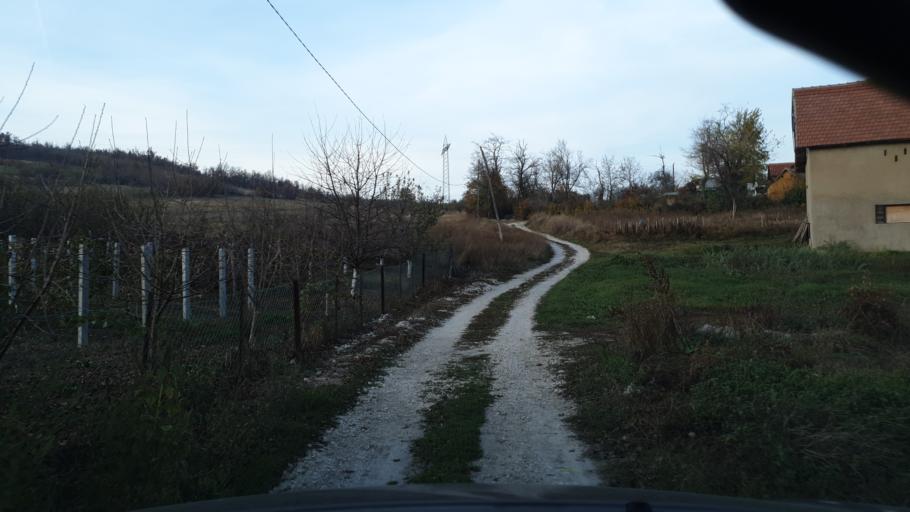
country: RS
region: Central Serbia
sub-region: Borski Okrug
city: Bor
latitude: 44.0608
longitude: 22.0898
